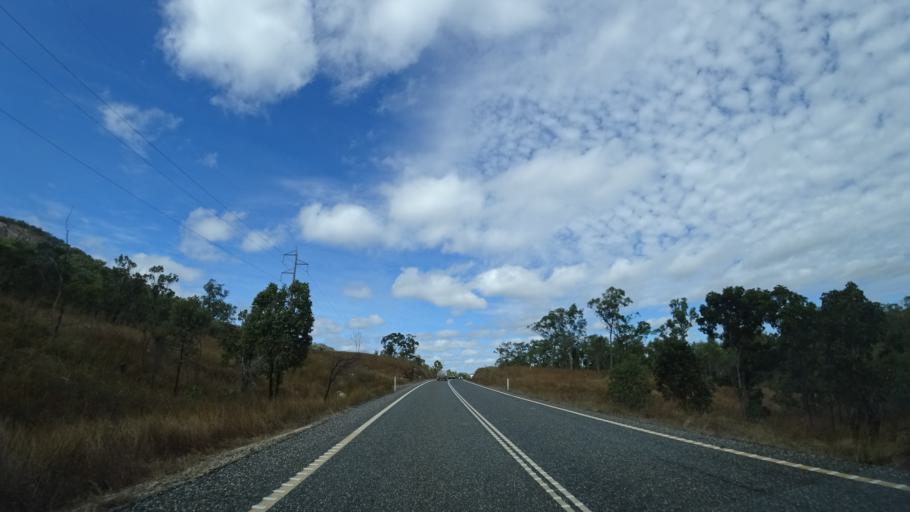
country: AU
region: Queensland
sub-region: Cairns
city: Port Douglas
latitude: -16.3402
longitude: 144.7258
